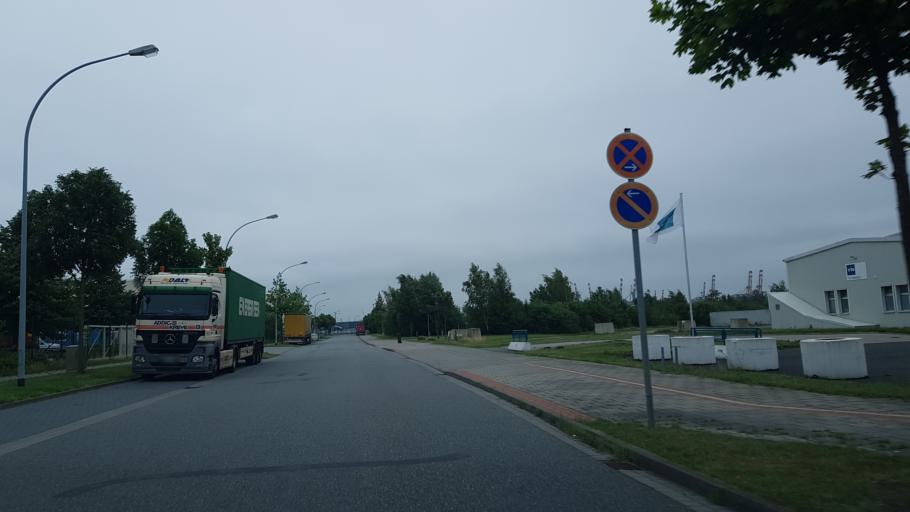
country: DE
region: Bremen
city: Bremerhaven
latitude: 53.5891
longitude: 8.5516
